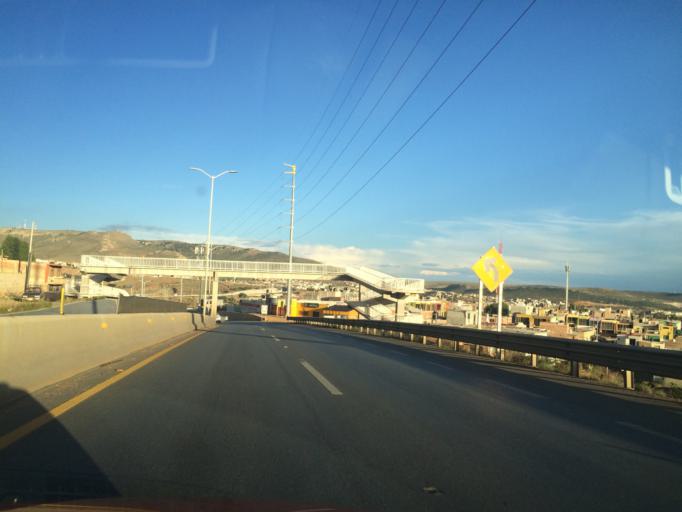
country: MX
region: Zacatecas
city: Zacatecas
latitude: 22.7584
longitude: -102.6011
